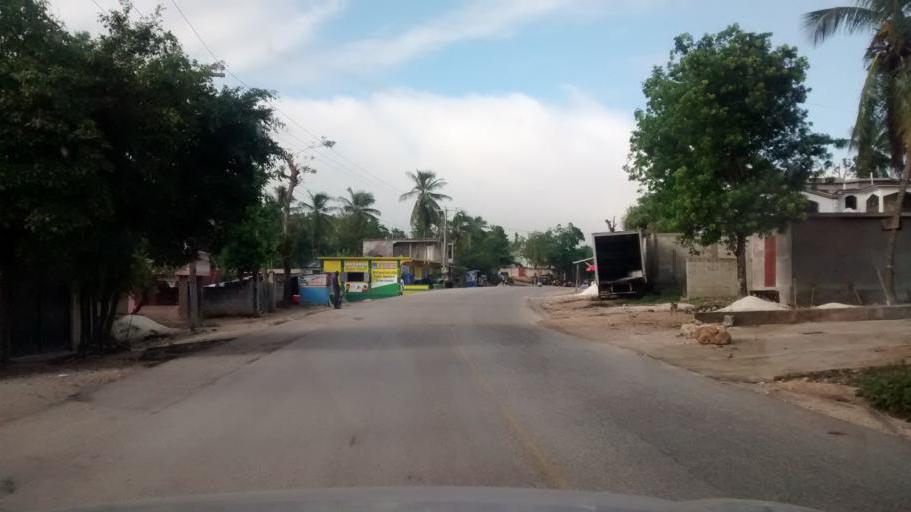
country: HT
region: Nippes
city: Miragoane
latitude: 18.3741
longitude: -73.1133
